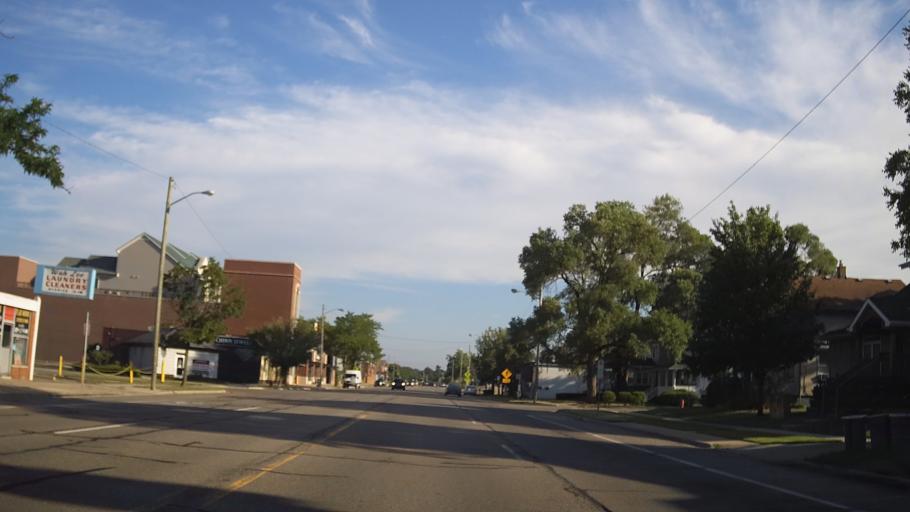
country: US
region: Michigan
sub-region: Oakland County
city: Royal Oak
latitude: 42.4819
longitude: -83.1466
